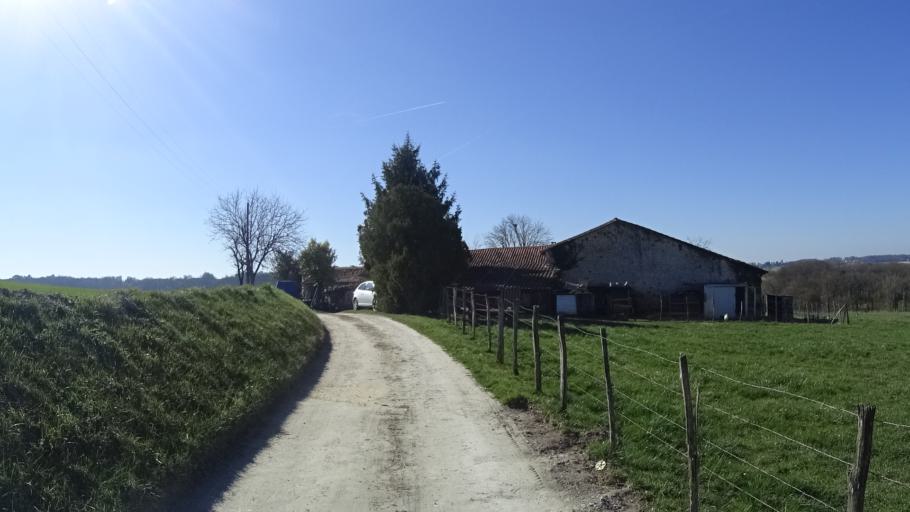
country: FR
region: Aquitaine
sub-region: Departement de la Dordogne
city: Riberac
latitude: 45.2281
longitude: 0.3374
